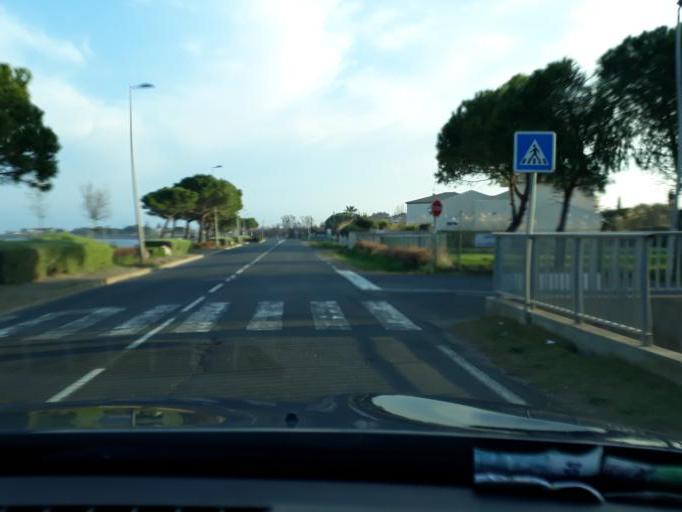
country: FR
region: Languedoc-Roussillon
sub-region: Departement de l'Herault
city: Marseillan
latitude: 43.3466
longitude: 3.5313
